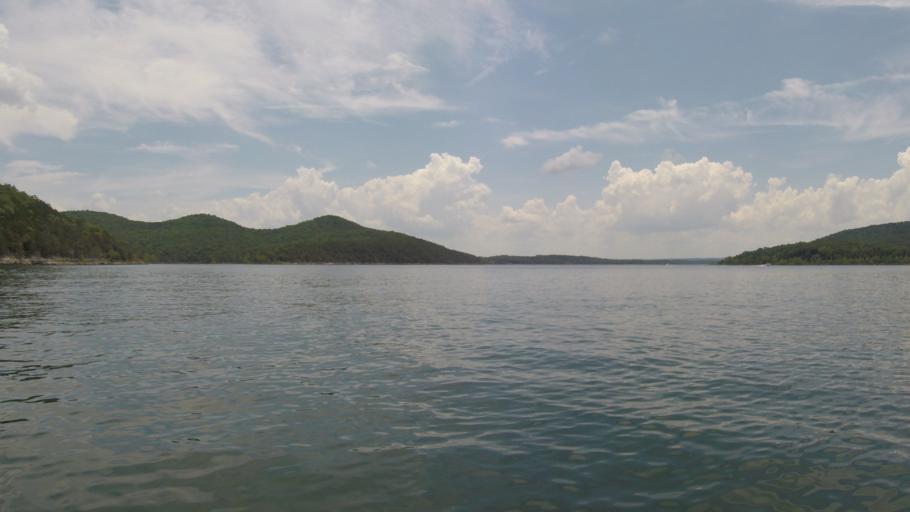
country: US
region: Missouri
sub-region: Barry County
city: Shell Knob
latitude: 36.6179
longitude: -93.5359
